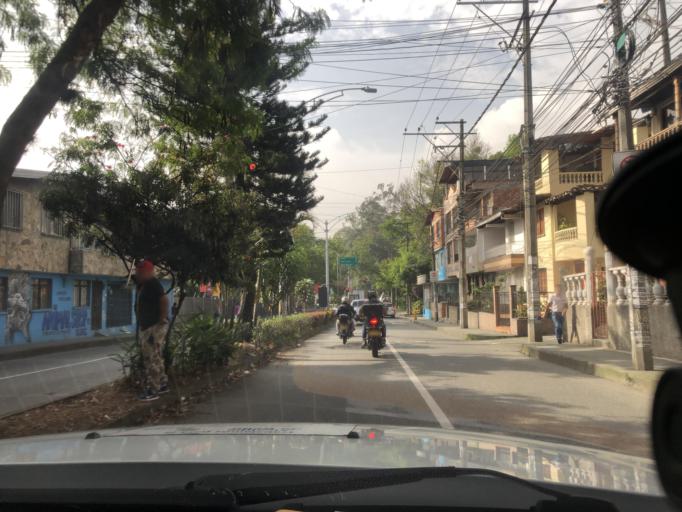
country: CO
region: Antioquia
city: Bello
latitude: 6.3316
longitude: -75.5624
